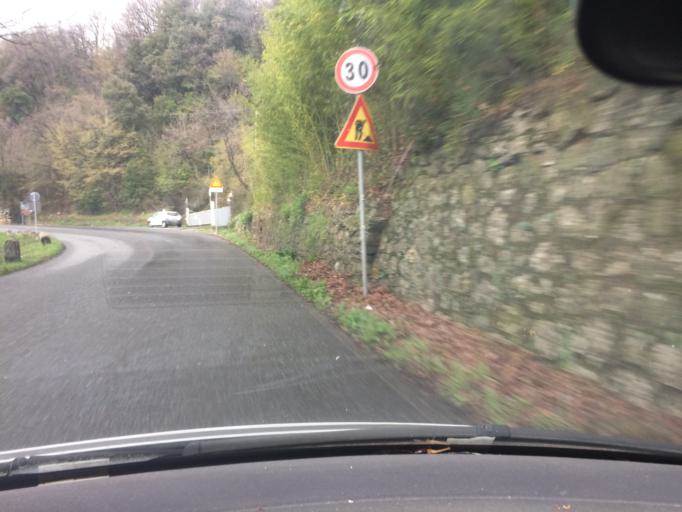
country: IT
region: Tuscany
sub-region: Provincia di Massa-Carrara
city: Massa
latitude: 44.0639
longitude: 10.1156
